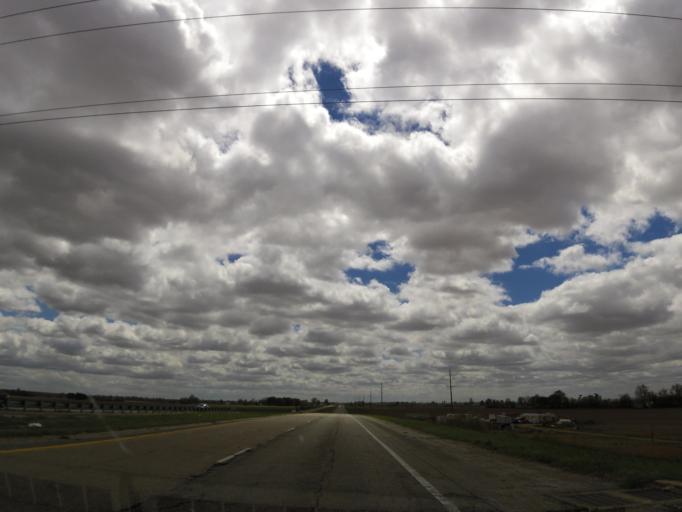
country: US
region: Arkansas
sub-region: Poinsett County
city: Trumann
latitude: 35.6204
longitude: -90.4968
